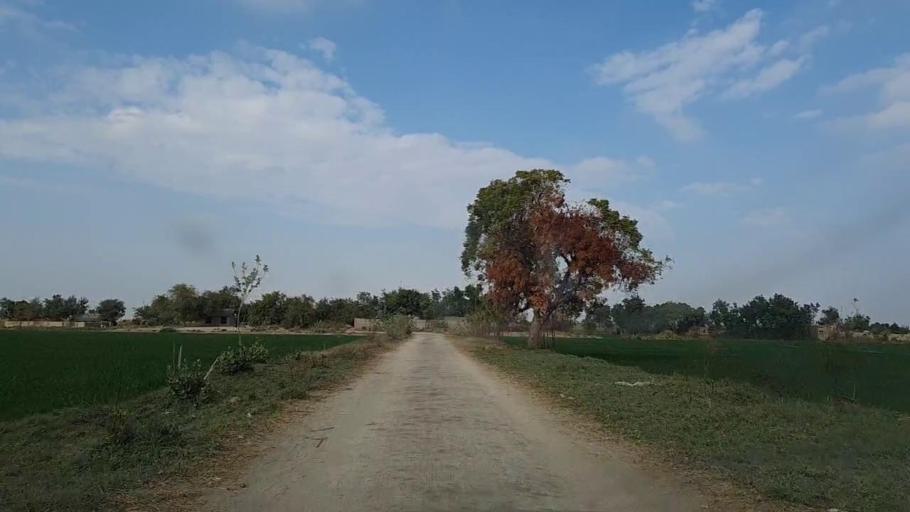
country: PK
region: Sindh
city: Sanghar
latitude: 26.2449
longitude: 69.0167
